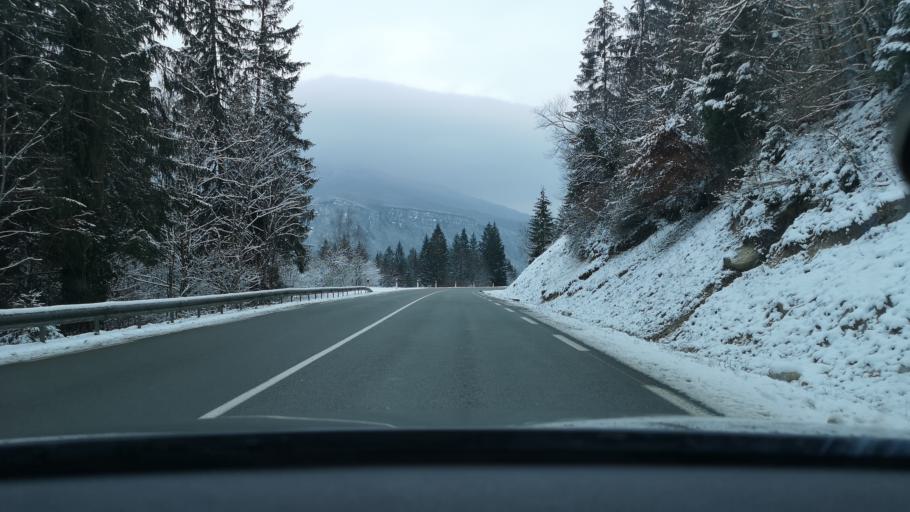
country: FR
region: Franche-Comte
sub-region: Departement du Jura
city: Moirans-en-Montagne
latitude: 46.3816
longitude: 5.7111
